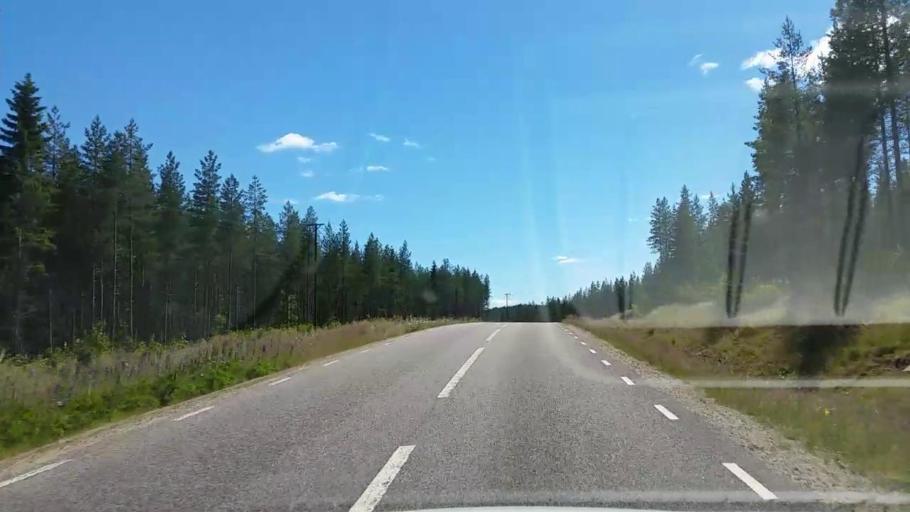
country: SE
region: Gaevleborg
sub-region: Ovanakers Kommun
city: Edsbyn
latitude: 61.5732
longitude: 15.6670
